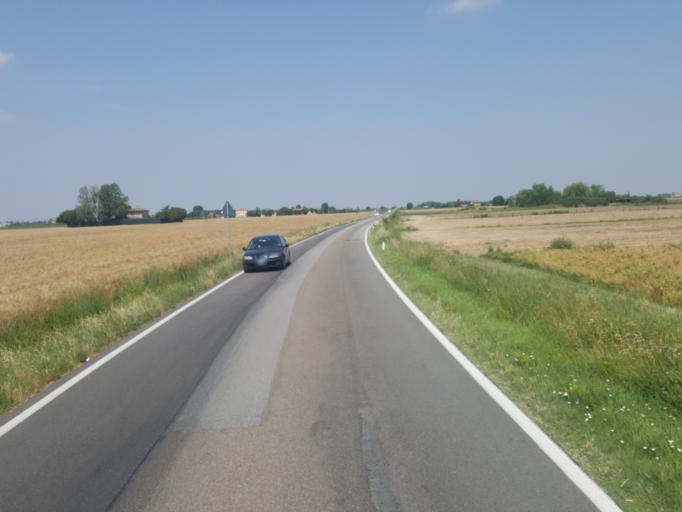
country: IT
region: Emilia-Romagna
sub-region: Provincia di Bologna
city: Castel Guelfo di Bologna
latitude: 44.4382
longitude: 11.6446
